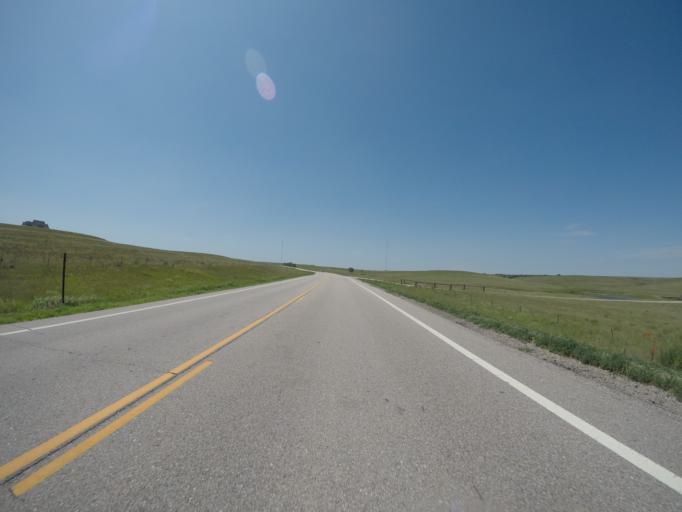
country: US
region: Kansas
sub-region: Osborne County
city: Osborne
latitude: 39.4917
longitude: -98.6963
